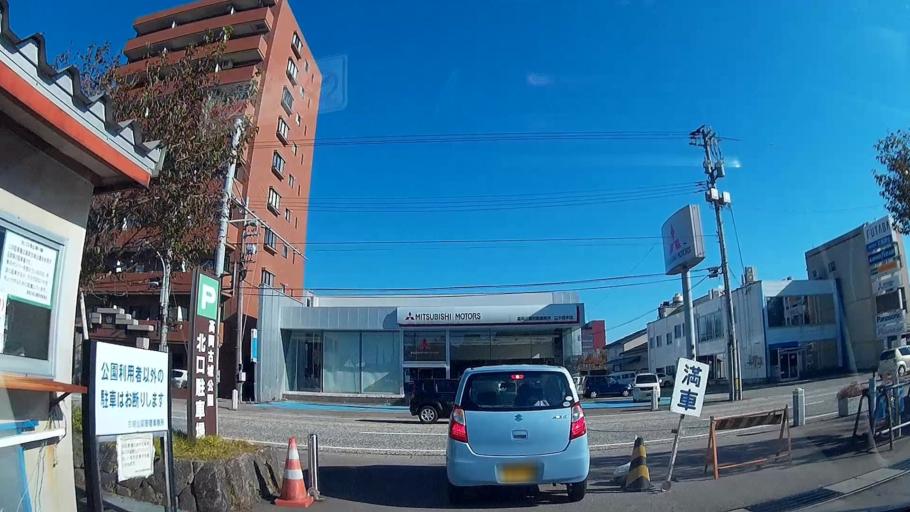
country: JP
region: Toyama
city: Takaoka
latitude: 36.7521
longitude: 137.0230
